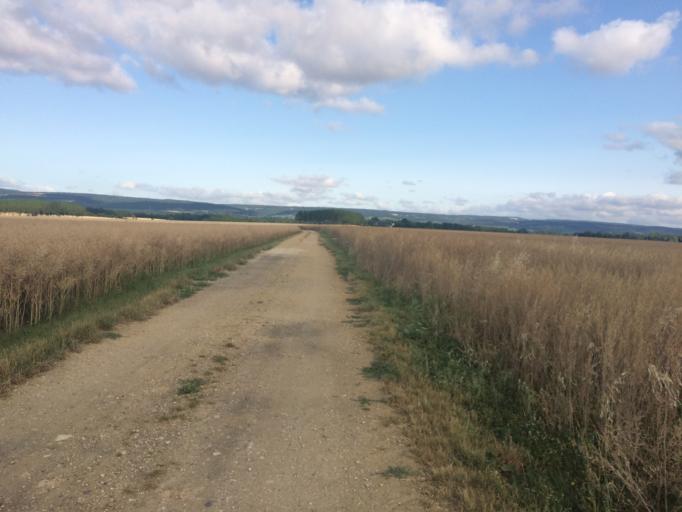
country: FR
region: Bourgogne
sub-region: Departement de la Cote-d'Or
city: Fenay
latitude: 47.2102
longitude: 5.0452
